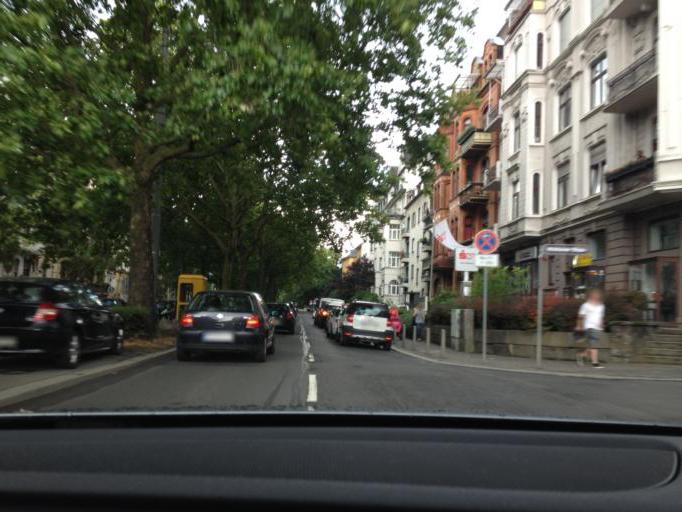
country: DE
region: Hesse
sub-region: Regierungsbezirk Darmstadt
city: Wiesbaden
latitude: 50.0771
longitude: 8.2208
